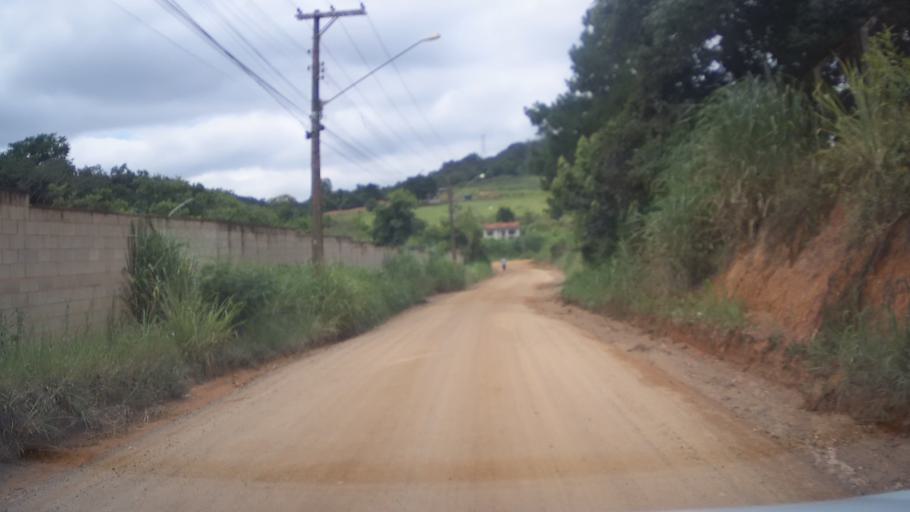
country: BR
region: Sao Paulo
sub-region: Louveira
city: Louveira
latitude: -23.0777
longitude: -46.9901
